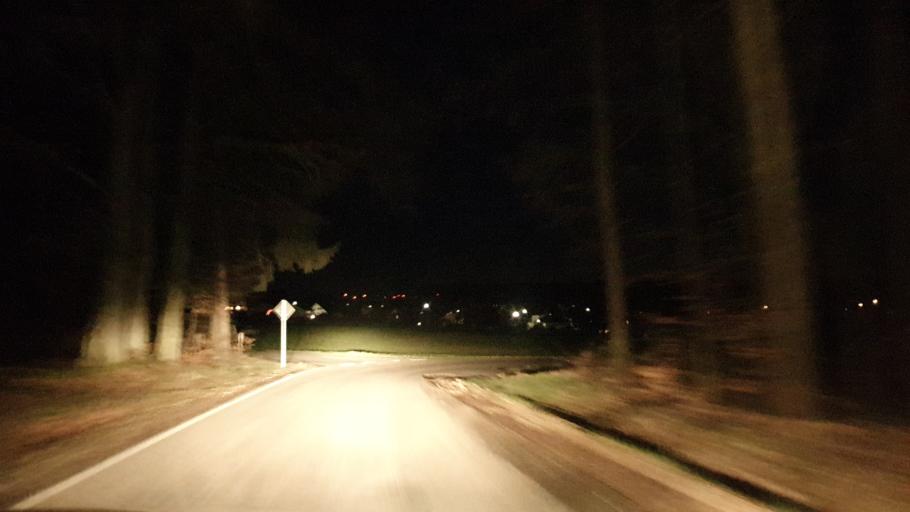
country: DE
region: Rheinland-Pfalz
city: Oberdreis
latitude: 50.6423
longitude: 7.6434
